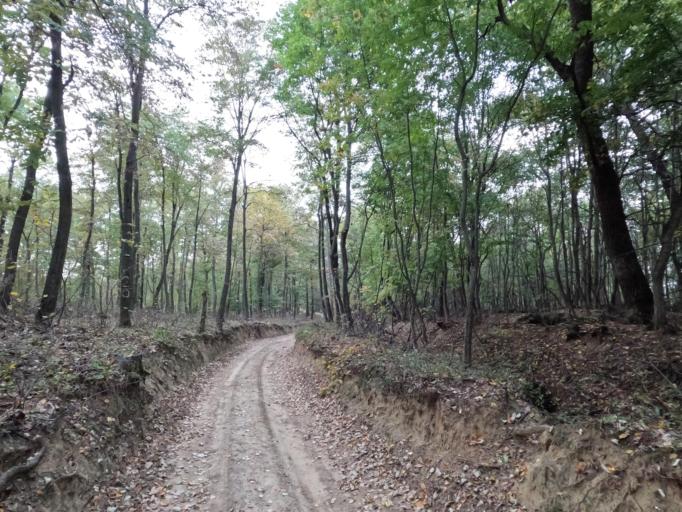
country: HU
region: Tolna
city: Szentgalpuszta
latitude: 46.3212
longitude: 18.6183
